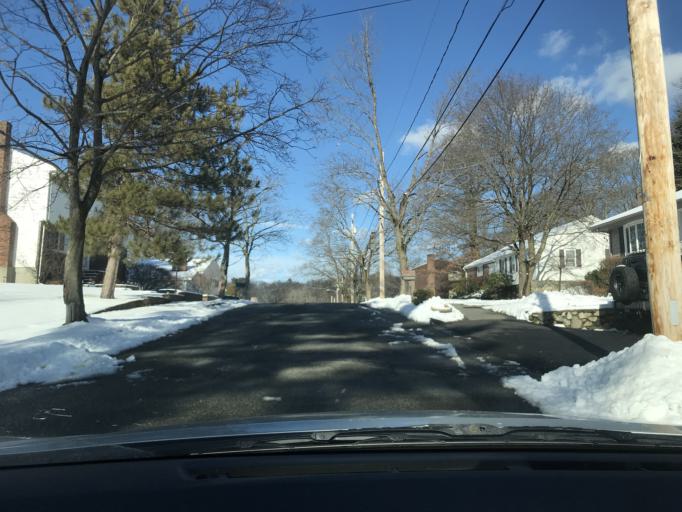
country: US
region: Massachusetts
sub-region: Essex County
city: Saugus
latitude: 42.4774
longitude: -71.0125
